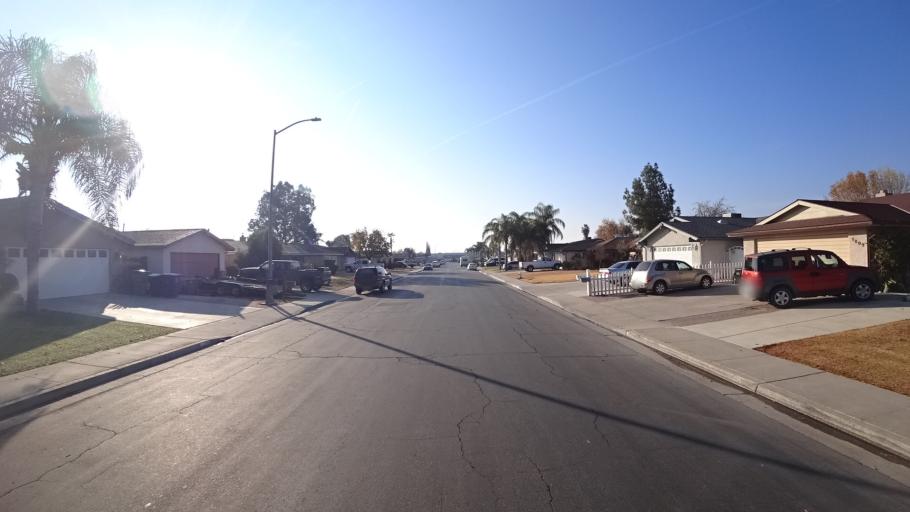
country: US
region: California
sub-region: Kern County
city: Greenfield
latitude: 35.3021
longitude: -119.0265
